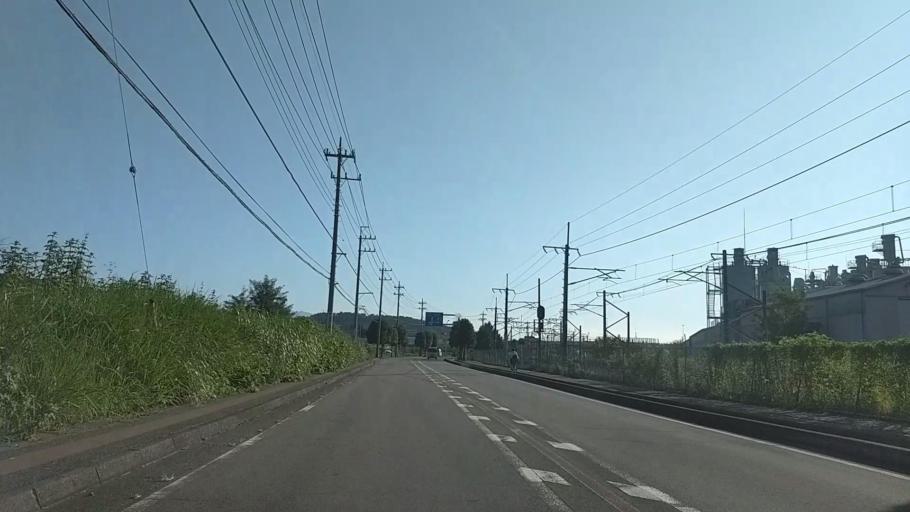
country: JP
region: Gunma
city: Annaka
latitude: 36.3309
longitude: 138.9092
